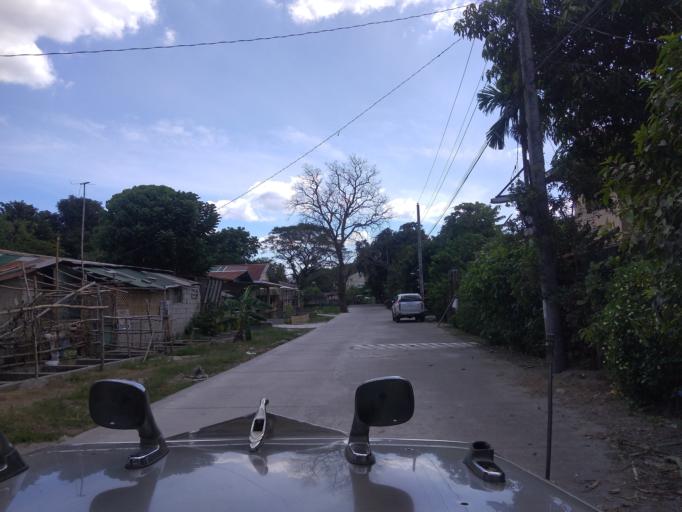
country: PH
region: Central Luzon
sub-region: Province of Pampanga
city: Santa Rita
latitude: 15.0074
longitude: 120.5911
